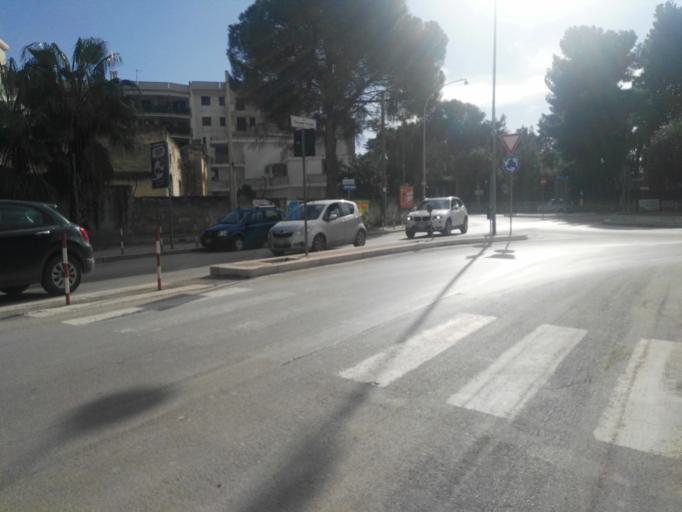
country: IT
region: Apulia
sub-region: Provincia di Barletta - Andria - Trani
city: Andria
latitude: 41.2195
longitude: 16.3062
